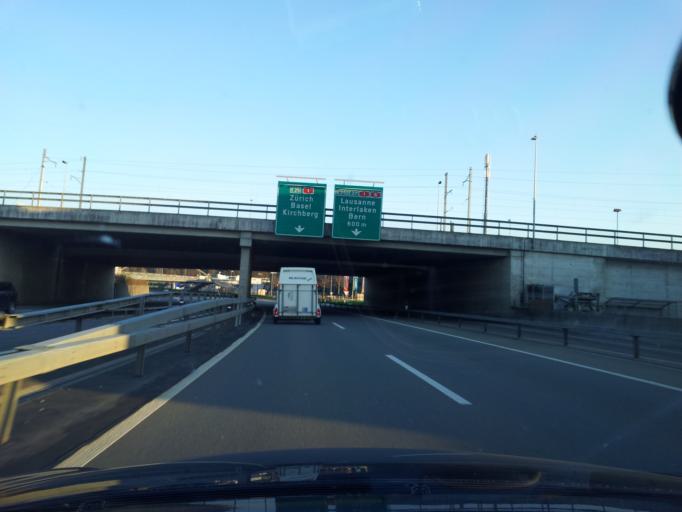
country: CH
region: Bern
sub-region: Bern-Mittelland District
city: Urtenen
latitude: 47.0184
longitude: 7.4892
